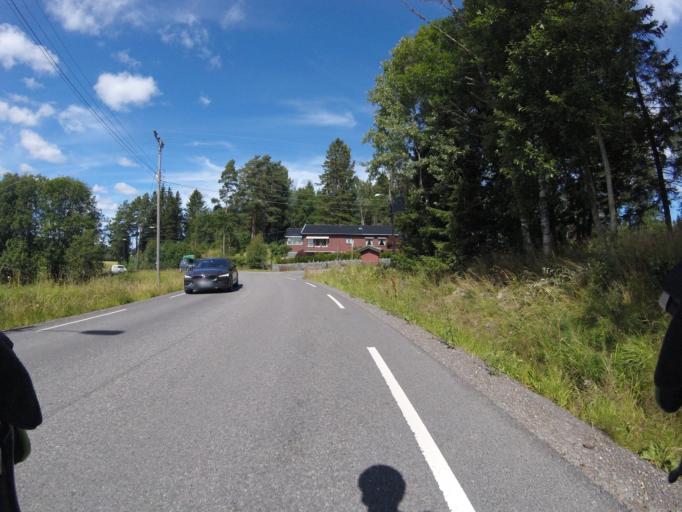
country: NO
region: Akershus
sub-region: Lorenskog
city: Kjenn
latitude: 59.9084
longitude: 10.9588
